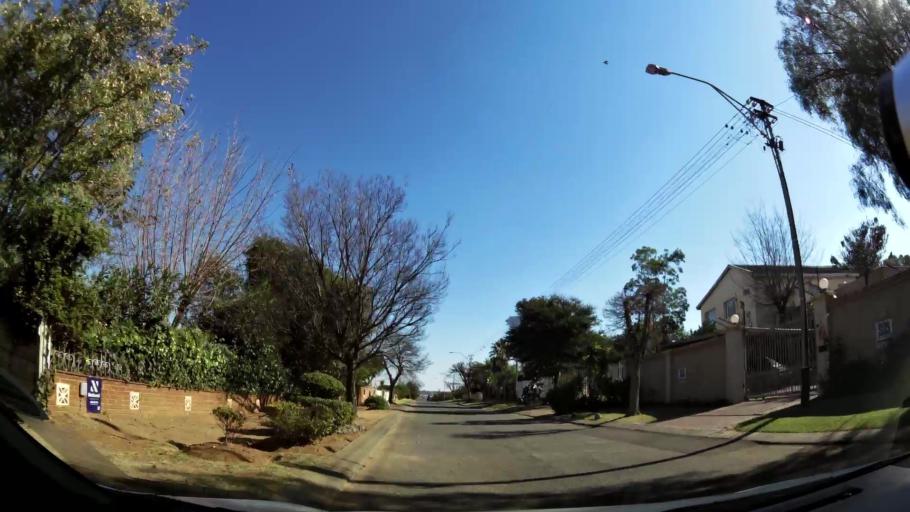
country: ZA
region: Gauteng
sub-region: City of Johannesburg Metropolitan Municipality
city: Johannesburg
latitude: -26.2717
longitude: 28.0195
